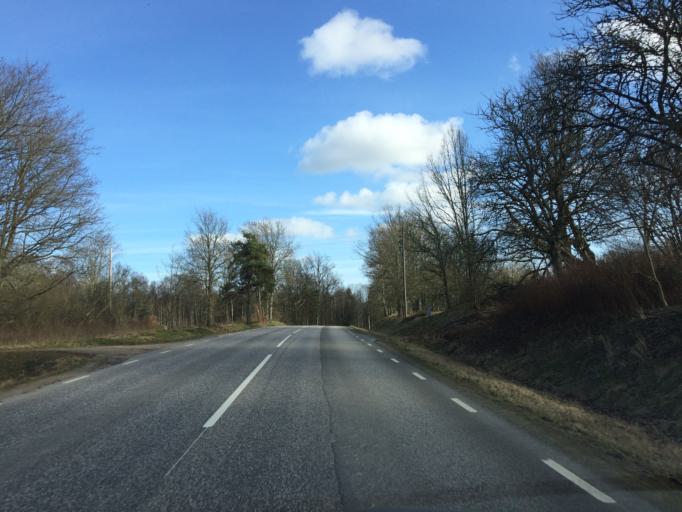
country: SE
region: Kronoberg
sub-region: Almhults Kommun
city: AElmhult
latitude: 56.5744
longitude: 14.1122
